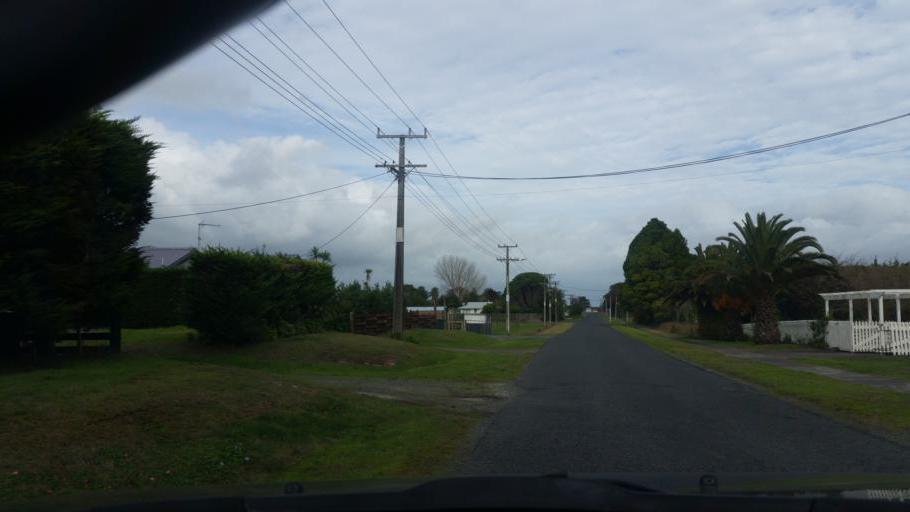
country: NZ
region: Northland
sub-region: Kaipara District
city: Dargaville
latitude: -36.0287
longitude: 173.9155
